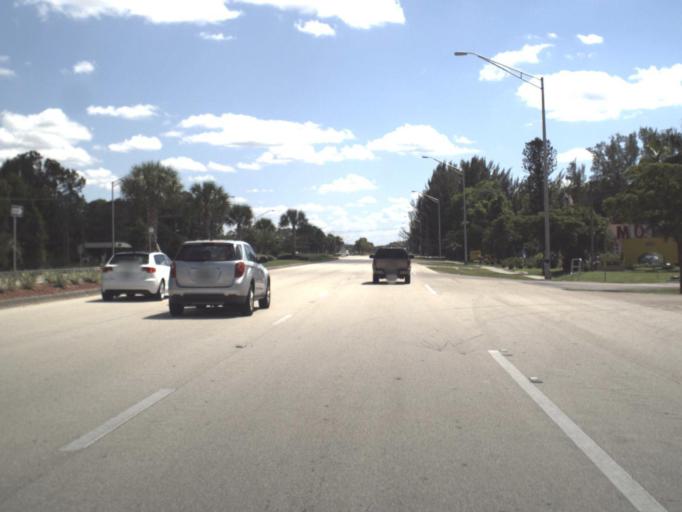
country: US
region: Florida
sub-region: Collier County
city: Naples Manor
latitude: 26.0878
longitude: -81.7305
